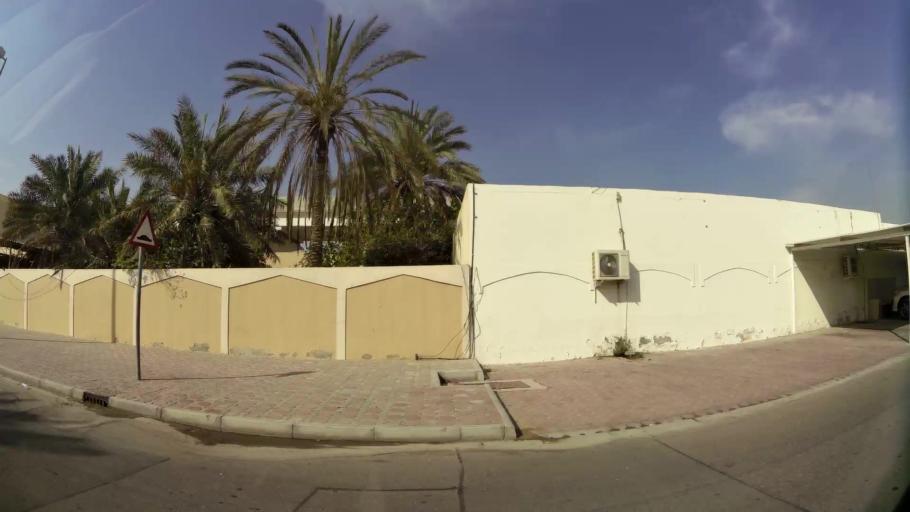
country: AE
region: Ash Shariqah
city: Sharjah
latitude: 25.2579
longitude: 55.3967
